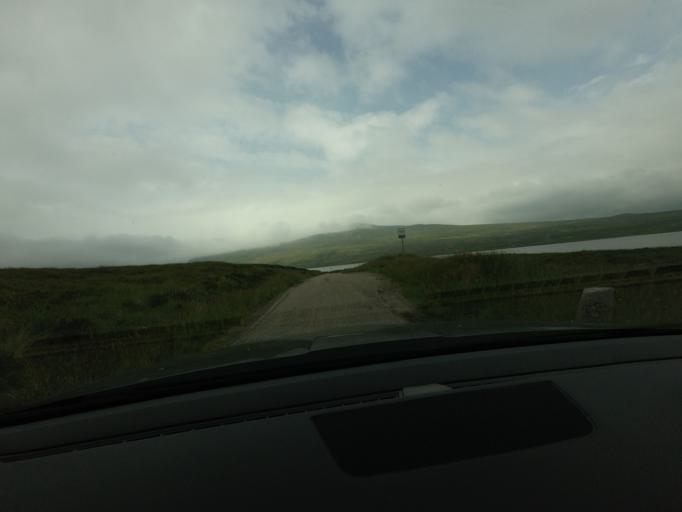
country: GB
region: Scotland
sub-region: Highland
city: Golspie
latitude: 58.3966
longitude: -4.3687
